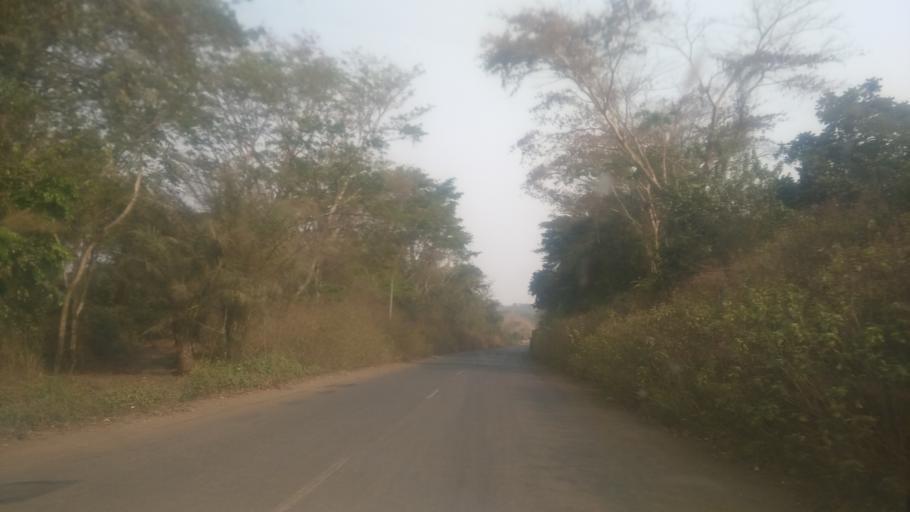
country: CM
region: West
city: Tonga
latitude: 5.0587
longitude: 10.6937
